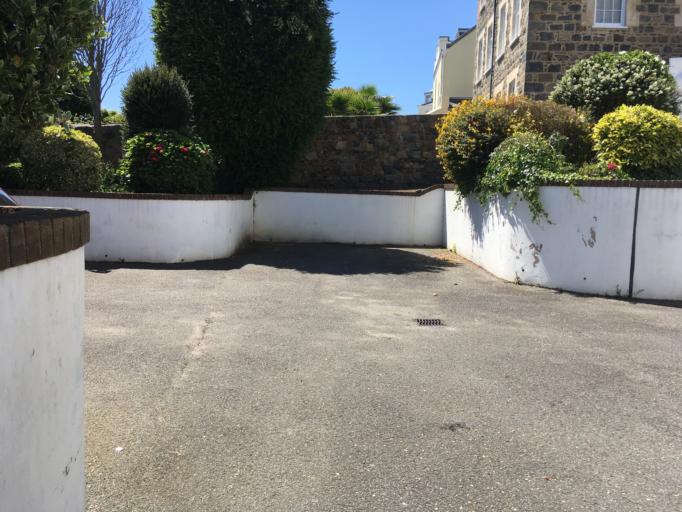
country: GG
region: St Peter Port
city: Saint Peter Port
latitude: 49.4555
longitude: -2.5471
